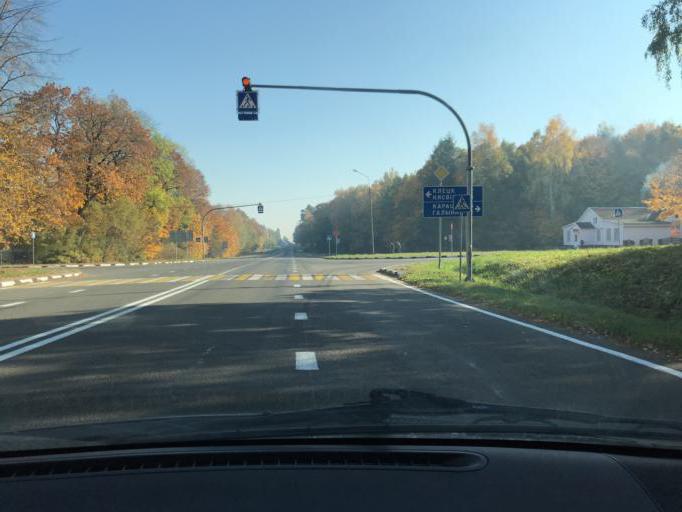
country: BY
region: Minsk
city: Klyetsk
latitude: 52.9691
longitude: 26.6196
